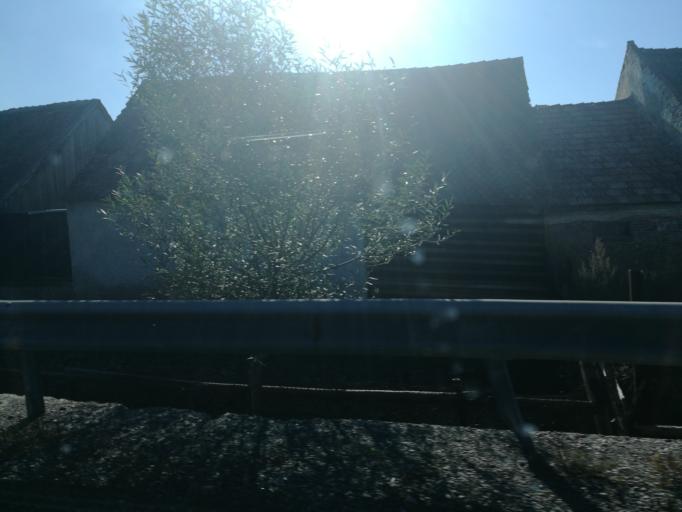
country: RO
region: Brasov
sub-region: Comuna Dumbravita
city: Dumbravita
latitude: 45.7686
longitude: 25.3626
